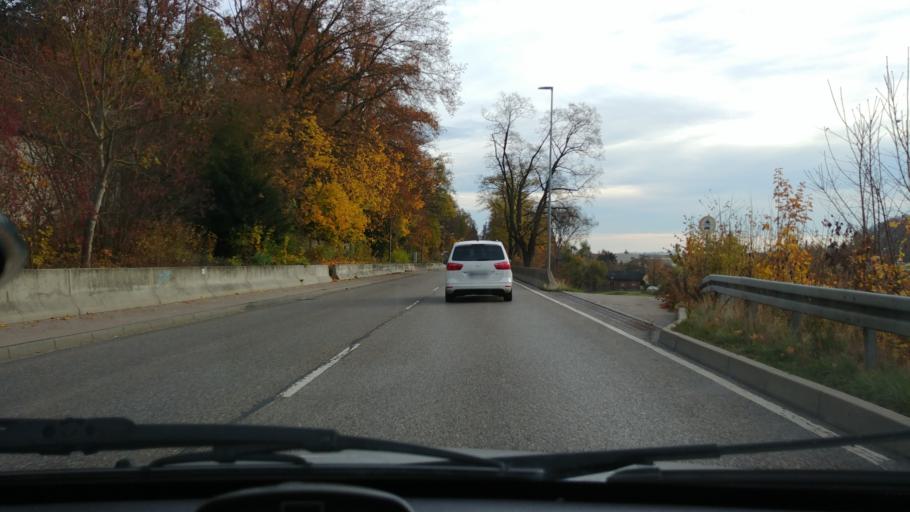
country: DE
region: Baden-Wuerttemberg
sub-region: Regierungsbezirk Stuttgart
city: Heidenheim an der Brenz
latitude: 48.6667
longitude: 10.1554
